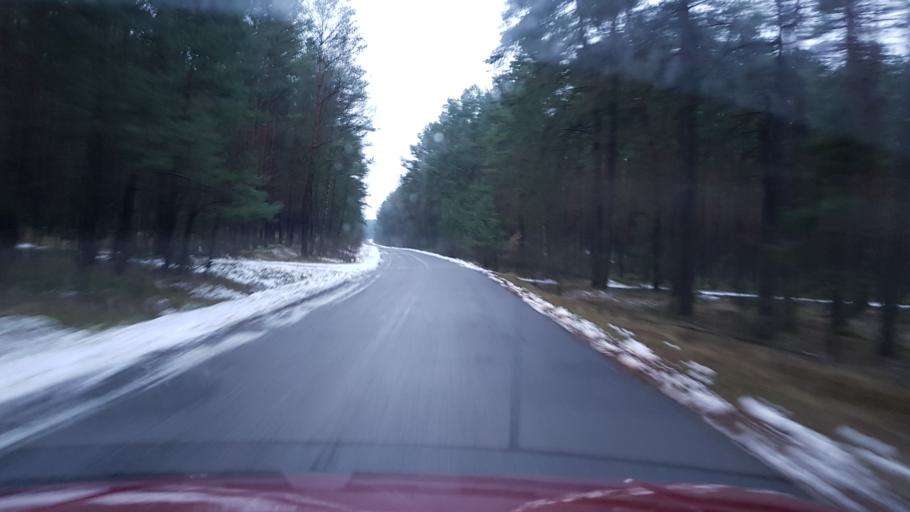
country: PL
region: West Pomeranian Voivodeship
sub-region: Powiat goleniowski
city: Goleniow
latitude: 53.4743
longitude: 14.8326
